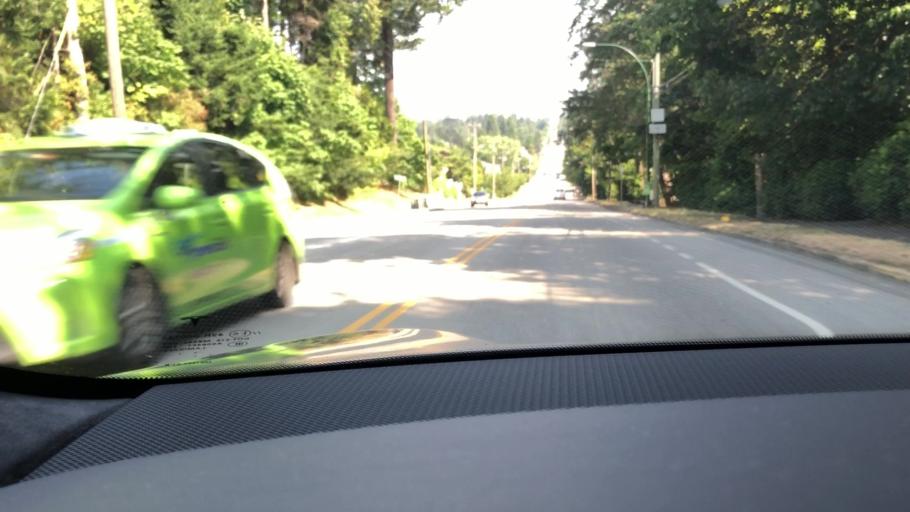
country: US
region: Washington
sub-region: Whatcom County
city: Point Roberts
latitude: 49.0055
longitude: -123.0686
